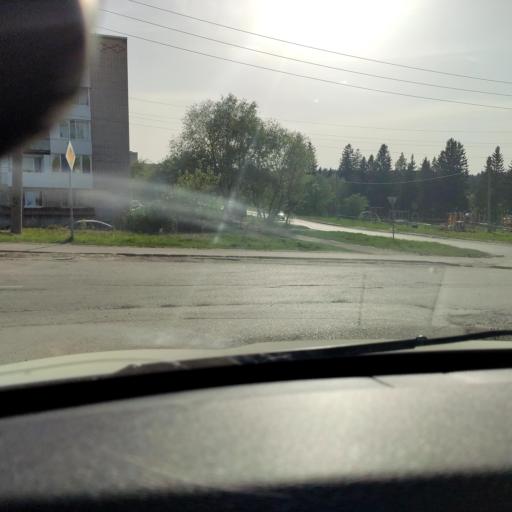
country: RU
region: Perm
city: Polazna
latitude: 58.2983
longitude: 56.3957
